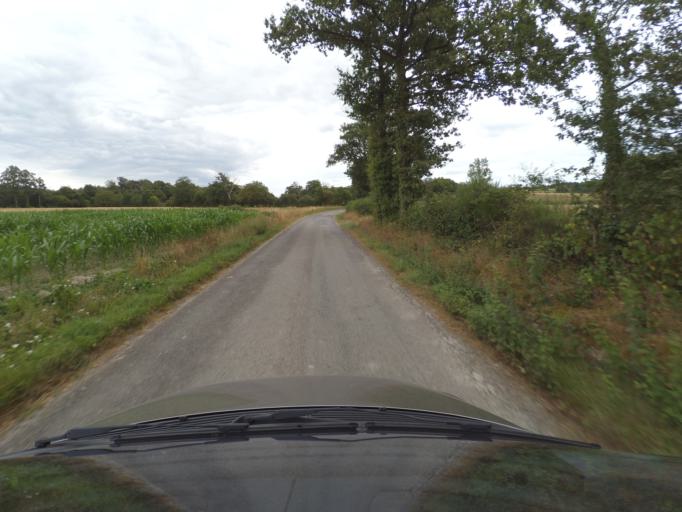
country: FR
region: Limousin
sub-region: Departement de la Haute-Vienne
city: Arnac-la-Poste
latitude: 46.2718
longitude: 1.2851
